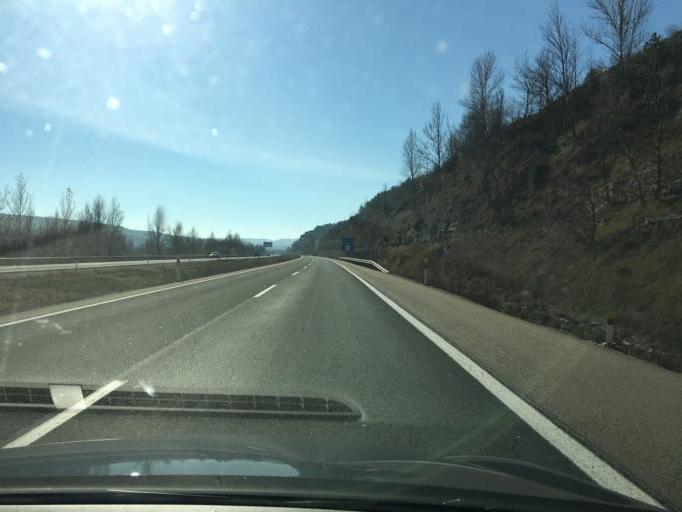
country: ES
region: Castille and Leon
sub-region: Provincia de Burgos
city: Pradanos de Bureba
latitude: 42.5201
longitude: -3.3405
